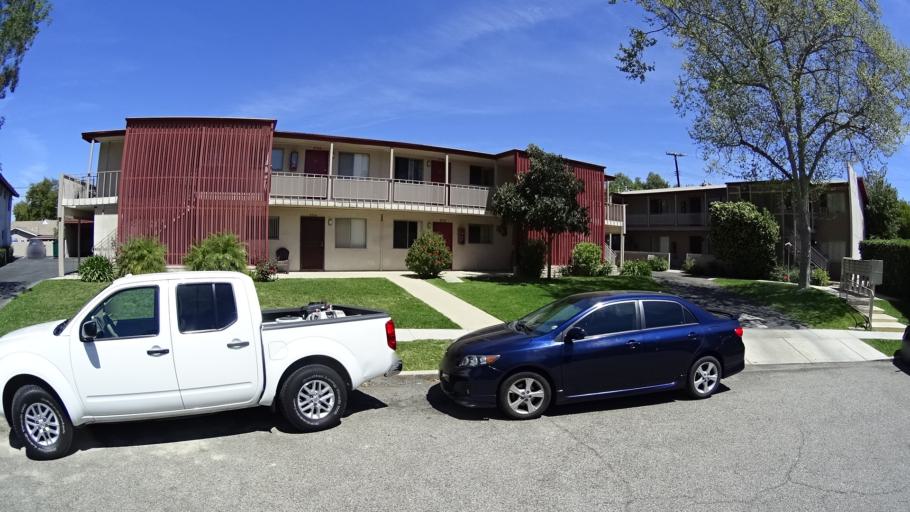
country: US
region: California
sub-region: Ventura County
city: Thousand Oaks
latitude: 34.2172
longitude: -118.8673
